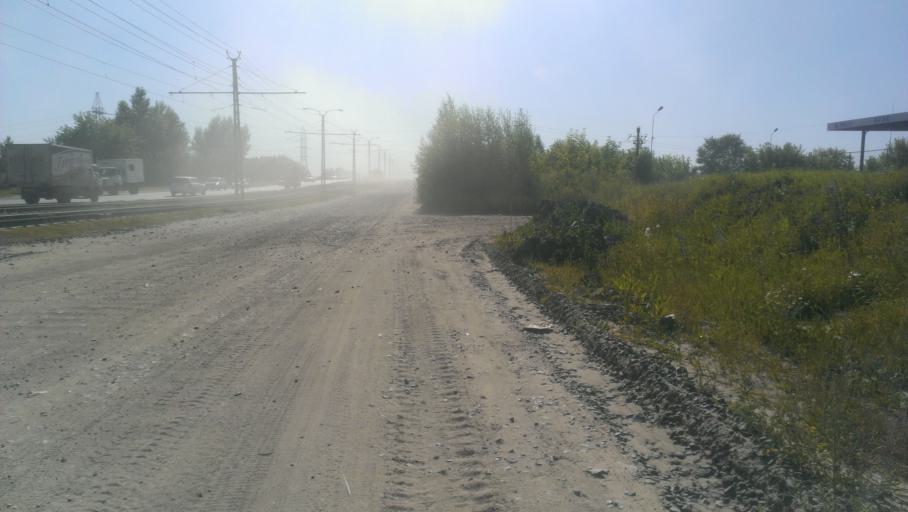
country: RU
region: Altai Krai
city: Novosilikatnyy
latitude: 53.3266
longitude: 83.6529
